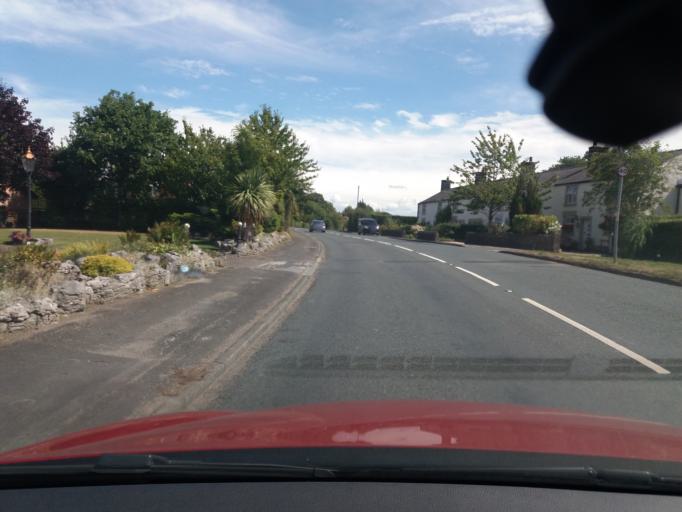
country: GB
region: England
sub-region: Lancashire
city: Euxton
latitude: 53.6603
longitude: -2.7017
